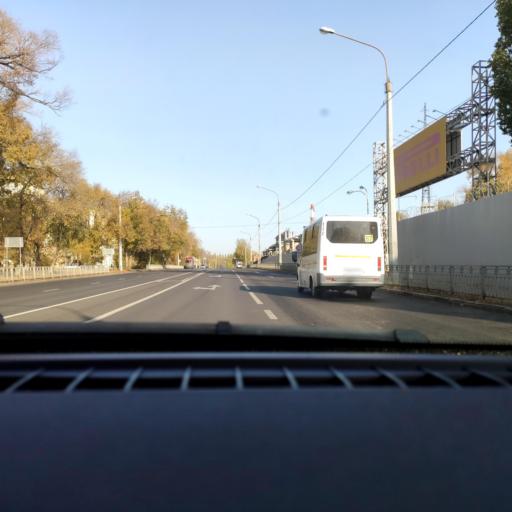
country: RU
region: Voronezj
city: Maslovka
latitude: 51.6015
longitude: 39.2439
